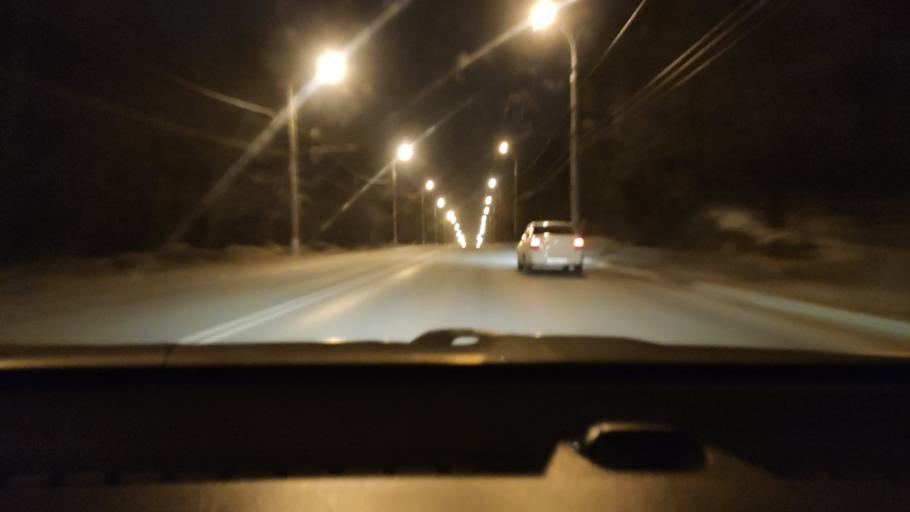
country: RU
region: Samara
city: Zhigulevsk
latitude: 53.4978
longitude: 49.5043
